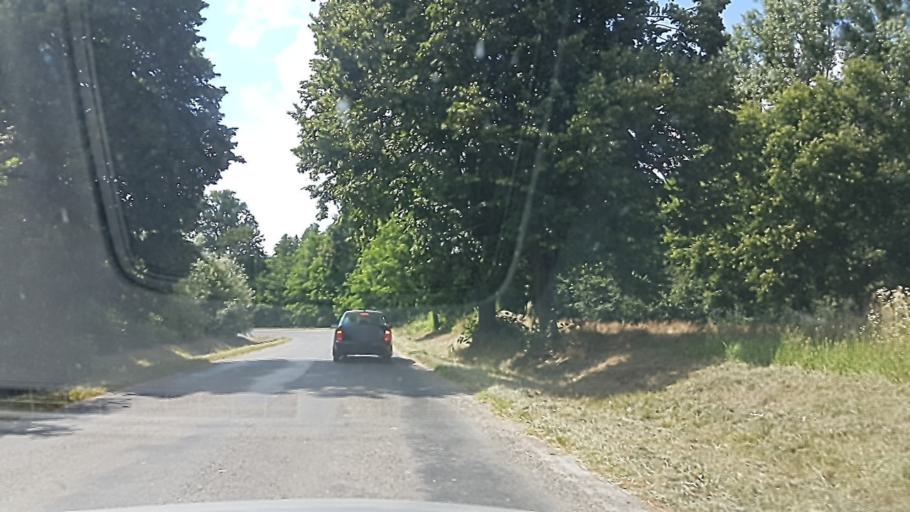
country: HU
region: Somogy
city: Barcs
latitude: 45.9605
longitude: 17.5946
